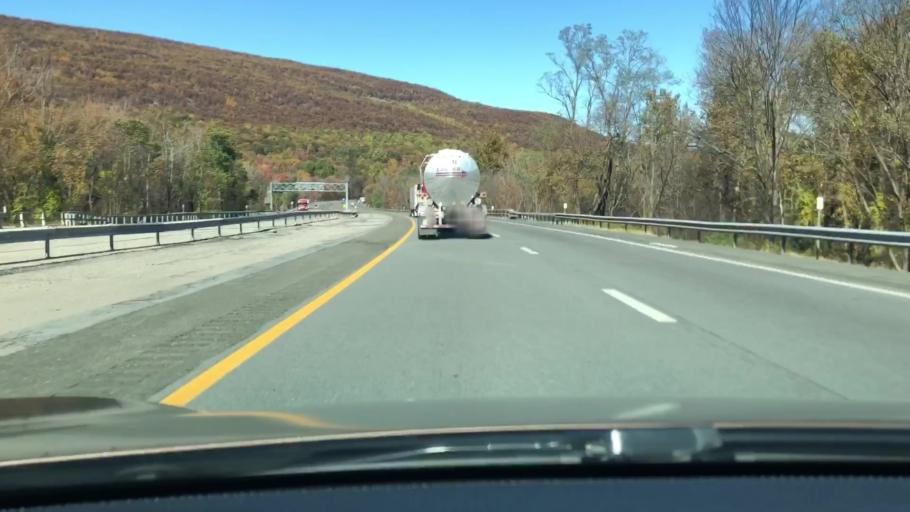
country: US
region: New York
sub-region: Orange County
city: Woodbury
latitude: 41.3711
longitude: -74.1015
